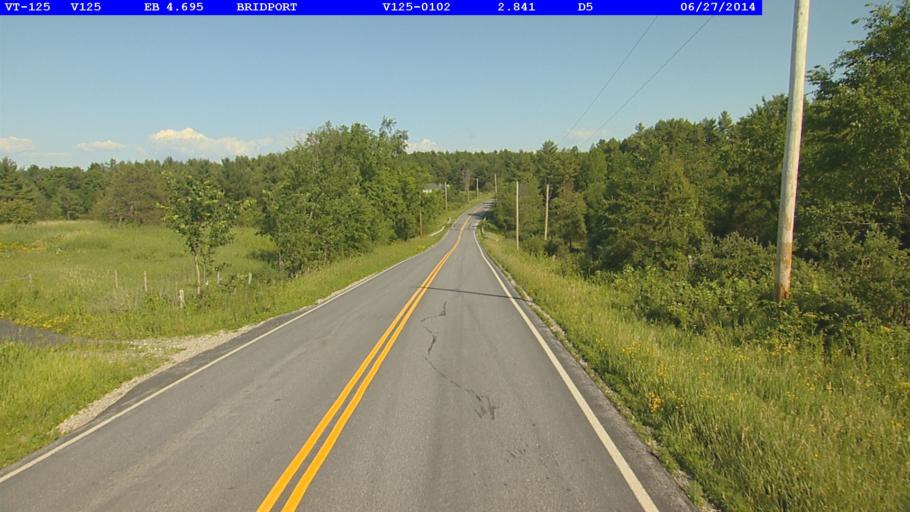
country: US
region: New York
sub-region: Essex County
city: Port Henry
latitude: 43.9980
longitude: -73.3538
